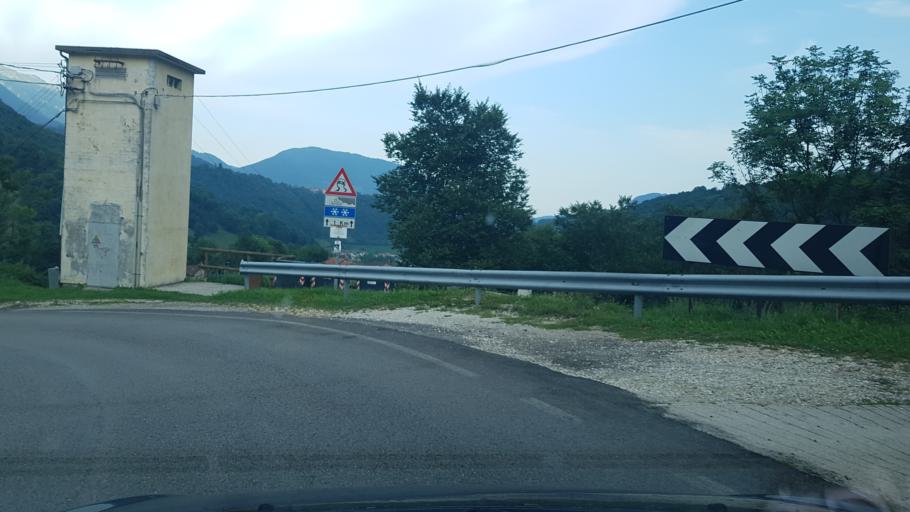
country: IT
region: Veneto
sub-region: Provincia di Vicenza
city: Valli del Pasubio
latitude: 45.7548
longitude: 11.2193
